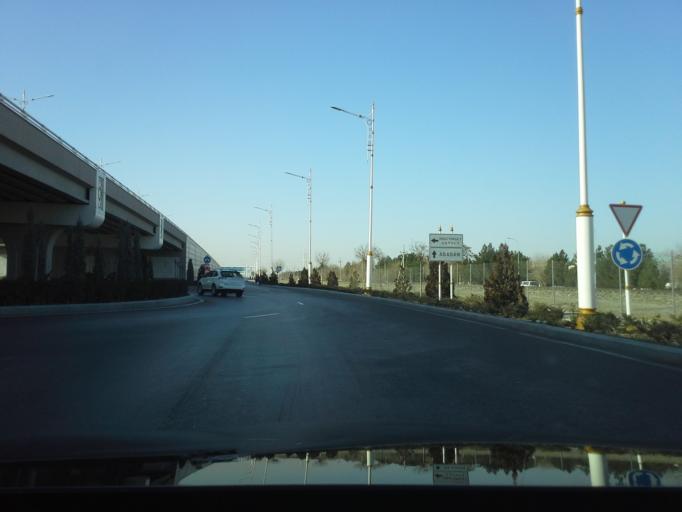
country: TM
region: Ahal
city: Ashgabat
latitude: 37.9623
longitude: 58.3629
